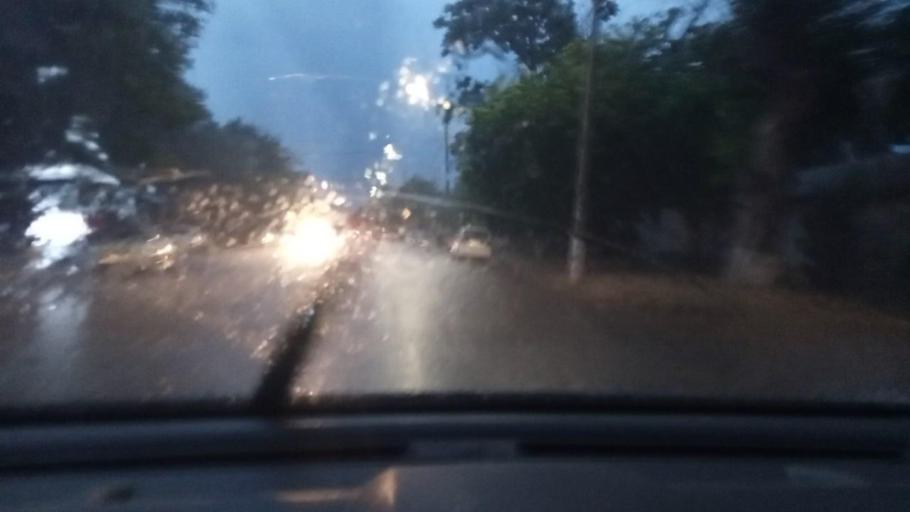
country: UZ
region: Toshkent
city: Salor
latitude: 41.3250
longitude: 69.3482
